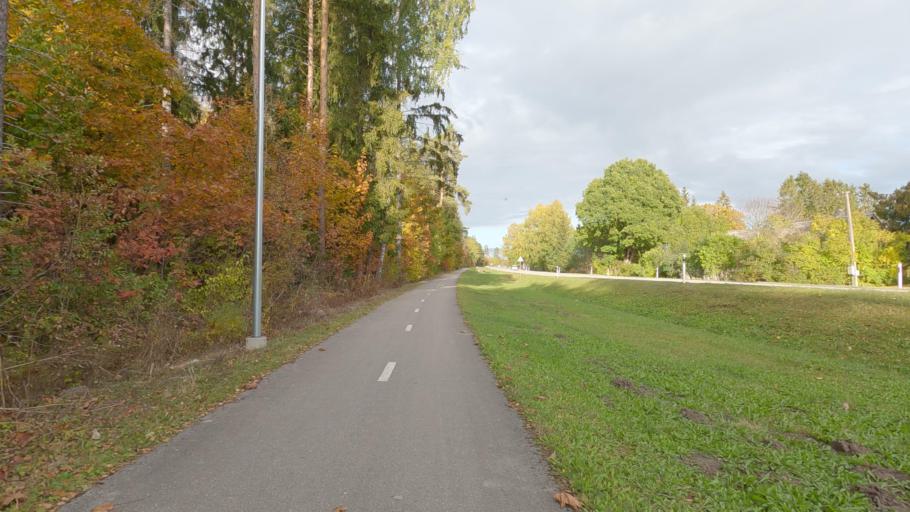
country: EE
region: Raplamaa
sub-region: Rapla vald
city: Rapla
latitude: 58.9392
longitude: 24.7479
